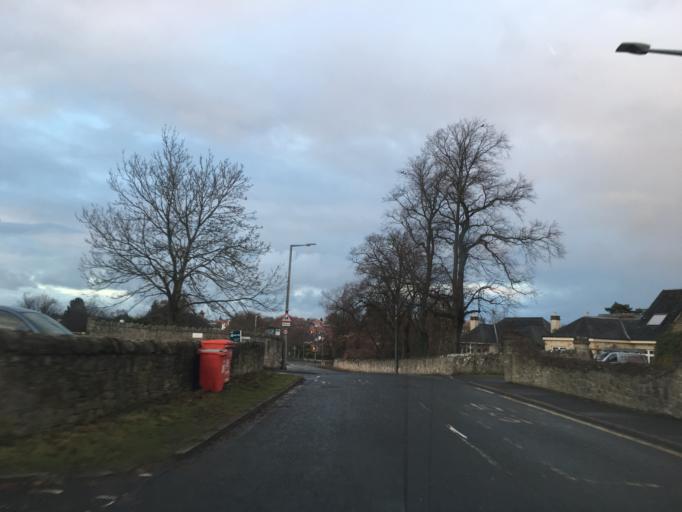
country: GB
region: Scotland
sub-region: Edinburgh
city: Colinton
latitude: 55.9547
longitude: -3.2579
